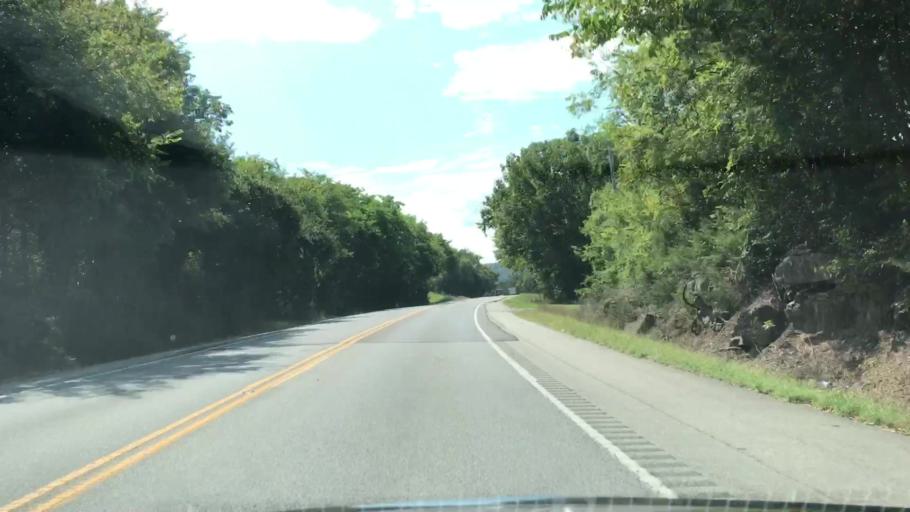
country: US
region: Tennessee
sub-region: Smith County
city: Carthage
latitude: 36.3300
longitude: -86.0228
